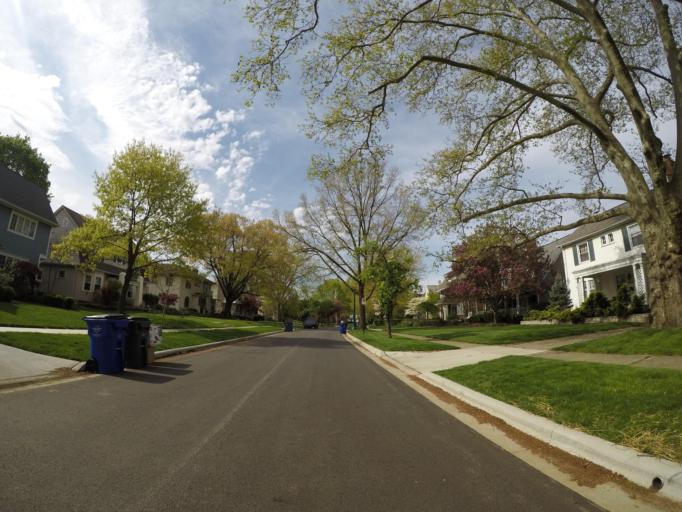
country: US
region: Ohio
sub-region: Franklin County
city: Upper Arlington
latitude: 39.9935
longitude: -83.0581
